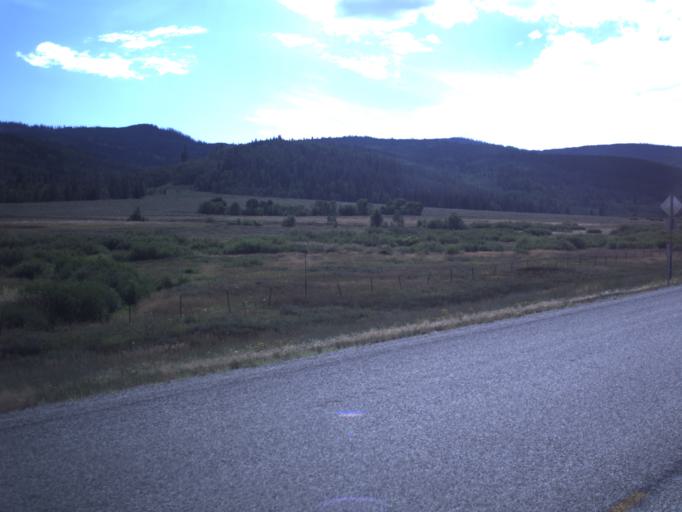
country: US
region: Utah
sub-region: Wasatch County
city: Heber
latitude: 40.2814
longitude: -111.2278
